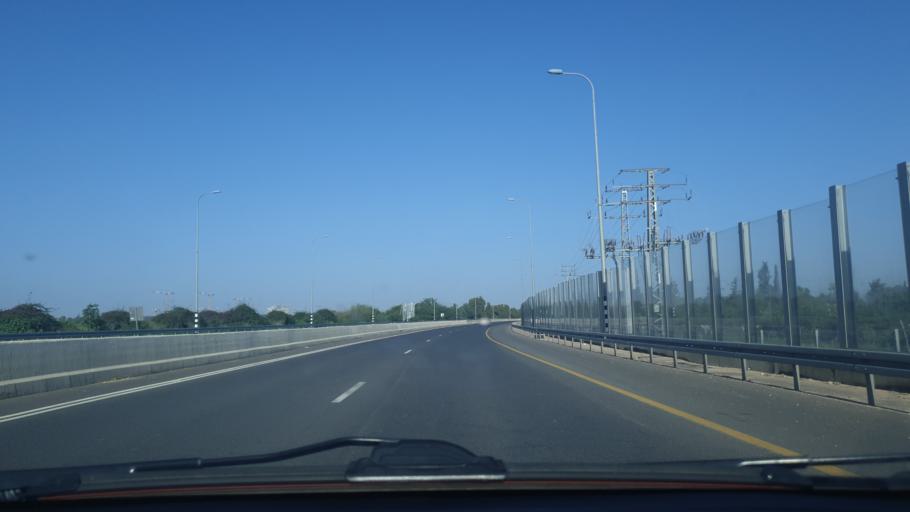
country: IL
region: Central District
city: Ramla
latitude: 31.9457
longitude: 34.8606
